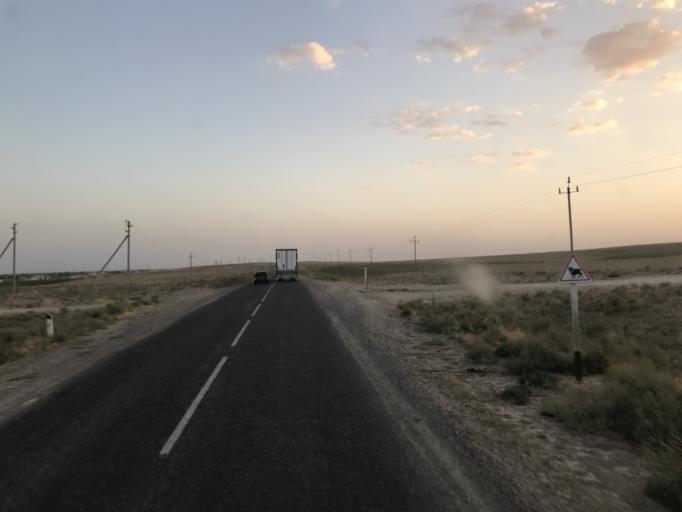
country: UZ
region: Toshkent
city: Amir Timur
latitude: 41.3482
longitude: 68.7074
